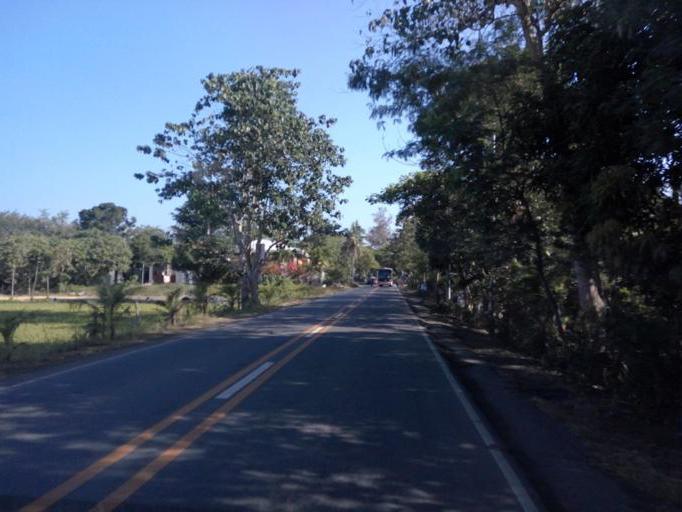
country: PH
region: Cagayan Valley
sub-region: Province of Cagayan
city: Amulung
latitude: 17.8227
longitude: 121.7258
